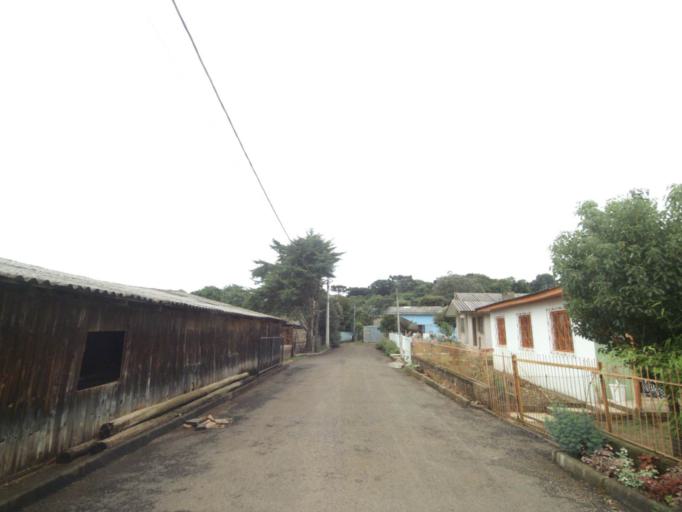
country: BR
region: Rio Grande do Sul
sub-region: Lagoa Vermelha
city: Lagoa Vermelha
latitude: -28.2196
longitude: -51.5219
